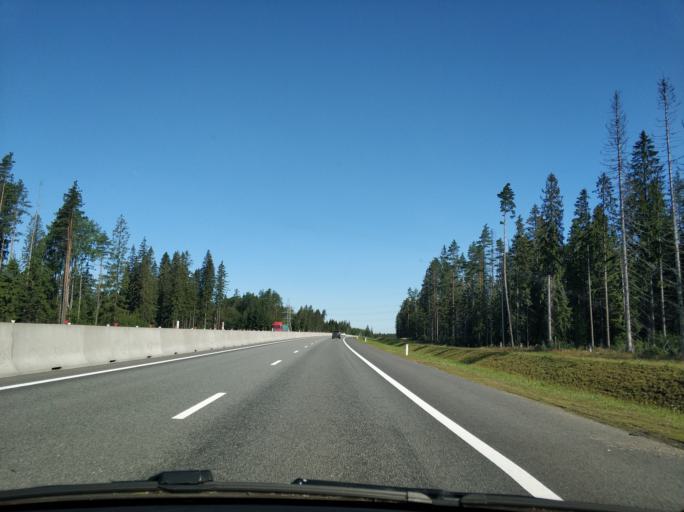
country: RU
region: Leningrad
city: Sosnovo
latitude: 60.5215
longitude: 30.1719
